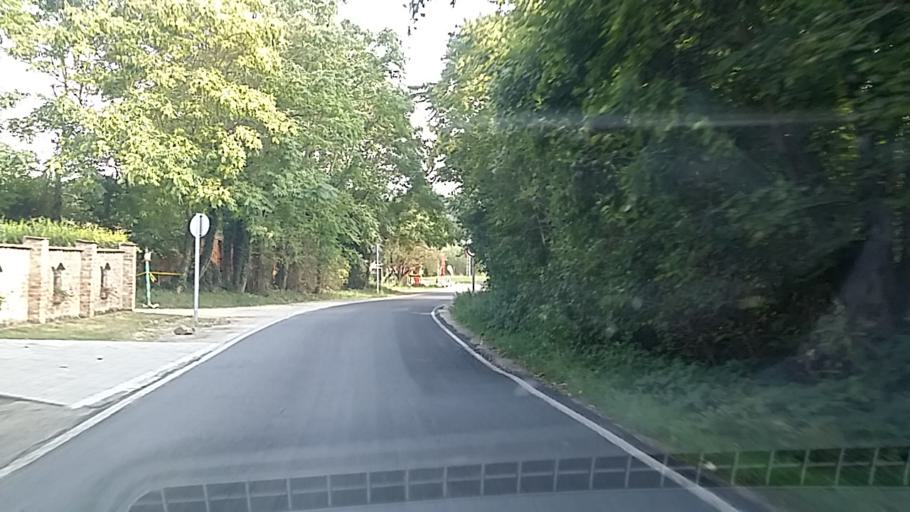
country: HU
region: Gyor-Moson-Sopron
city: Fertorakos
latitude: 47.7273
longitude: 16.6233
